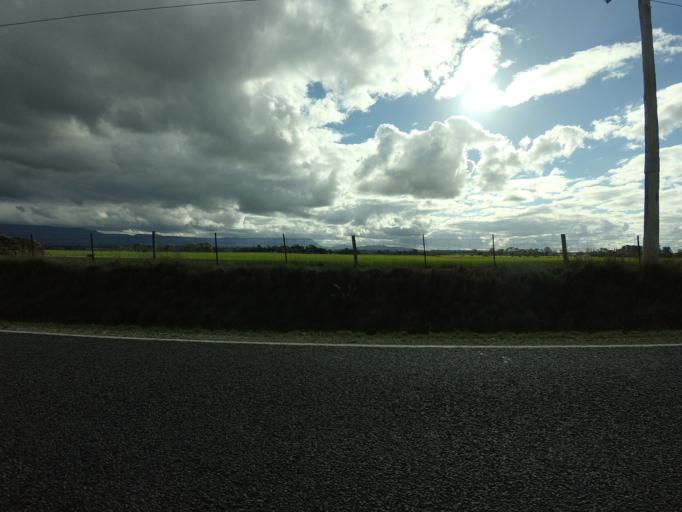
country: AU
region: Tasmania
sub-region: Northern Midlands
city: Longford
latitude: -41.7286
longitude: 147.0874
